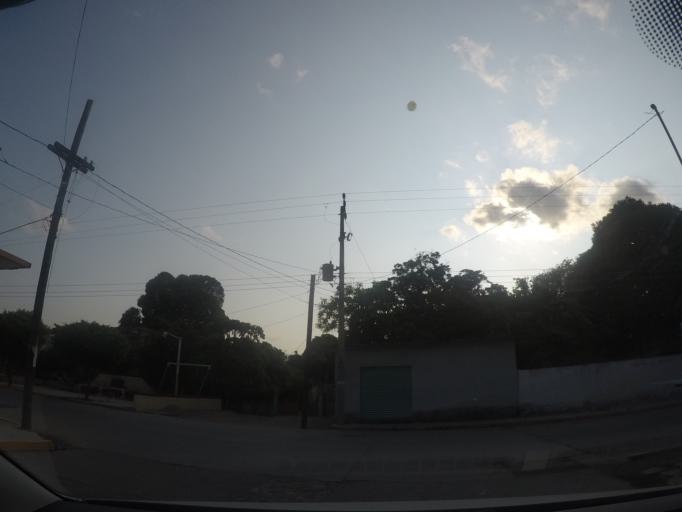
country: MX
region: Oaxaca
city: San Jeronimo Ixtepec
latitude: 16.5918
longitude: -95.1636
